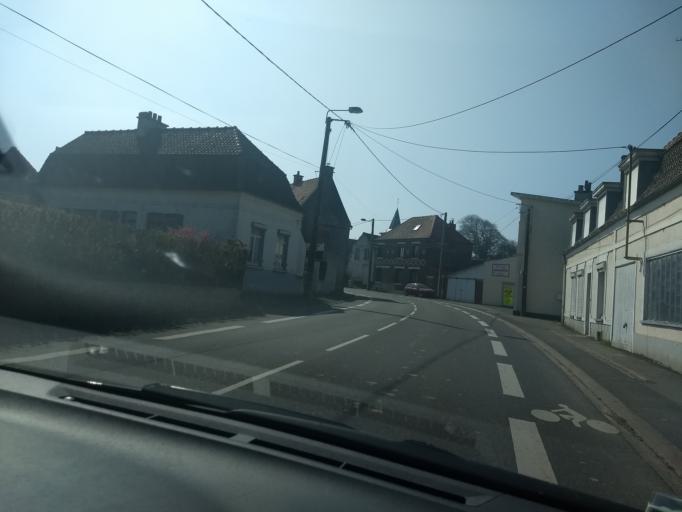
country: FR
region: Nord-Pas-de-Calais
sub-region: Departement du Pas-de-Calais
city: Tatinghem
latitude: 50.7435
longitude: 2.2069
